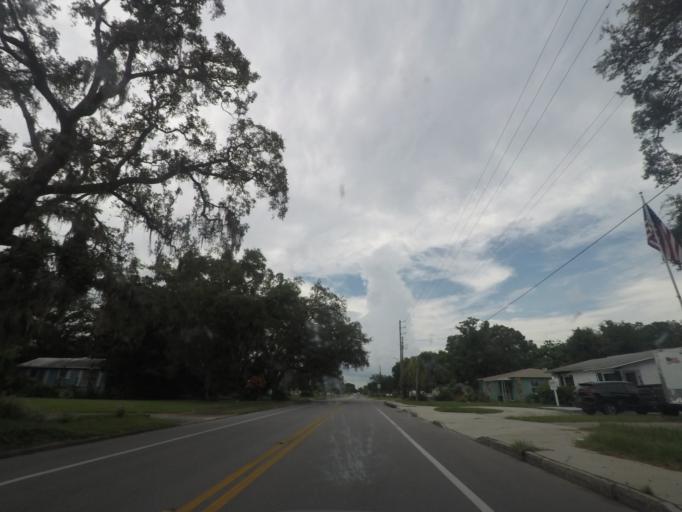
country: US
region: Florida
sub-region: Pinellas County
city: West and East Lealman
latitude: 27.7991
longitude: -82.6966
